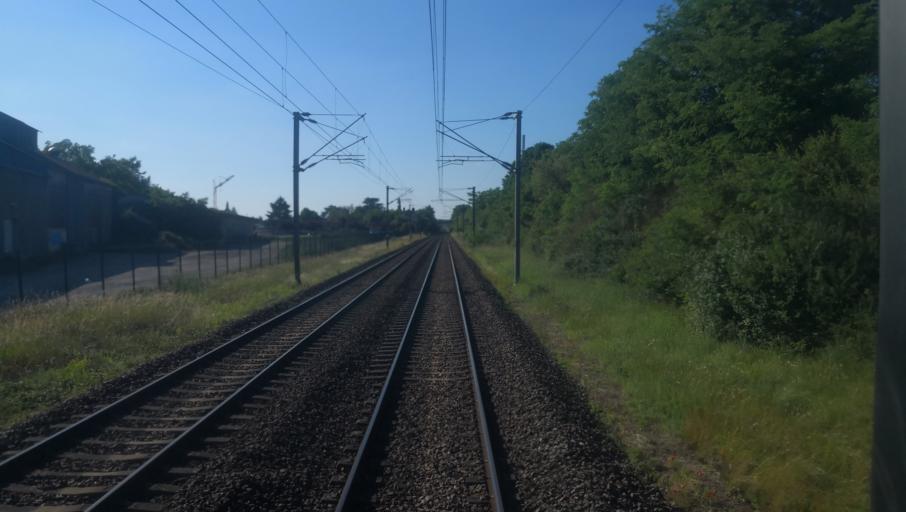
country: FR
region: Centre
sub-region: Departement du Loiret
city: Bonny-sur-Loire
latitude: 47.5568
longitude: 2.8461
